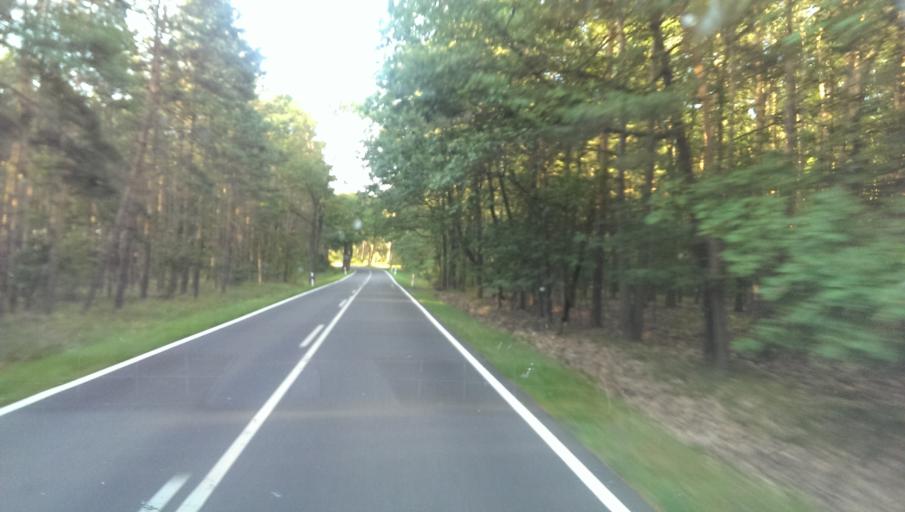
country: DE
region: Brandenburg
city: Trebbin
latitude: 52.2664
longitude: 13.2075
